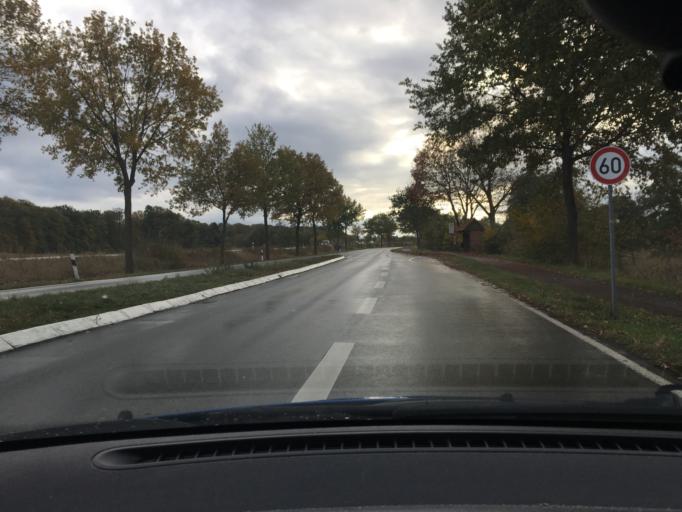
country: DE
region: Schleswig-Holstein
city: Fredeburg
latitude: 53.6453
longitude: 10.7012
